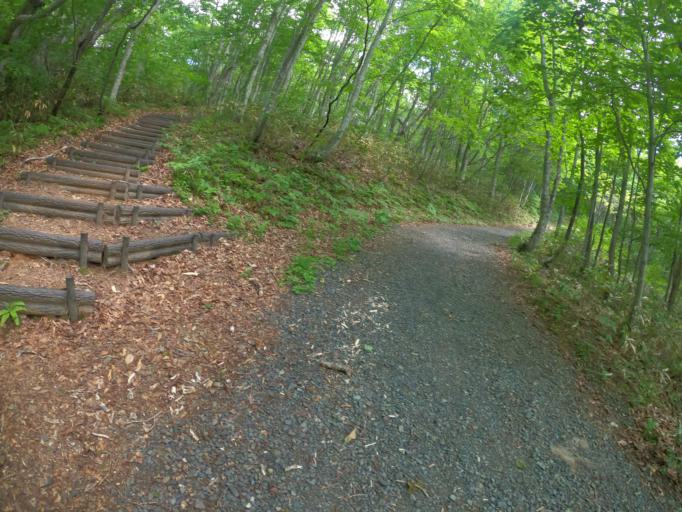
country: JP
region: Iwate
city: Ichinoseki
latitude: 38.9105
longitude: 140.8110
